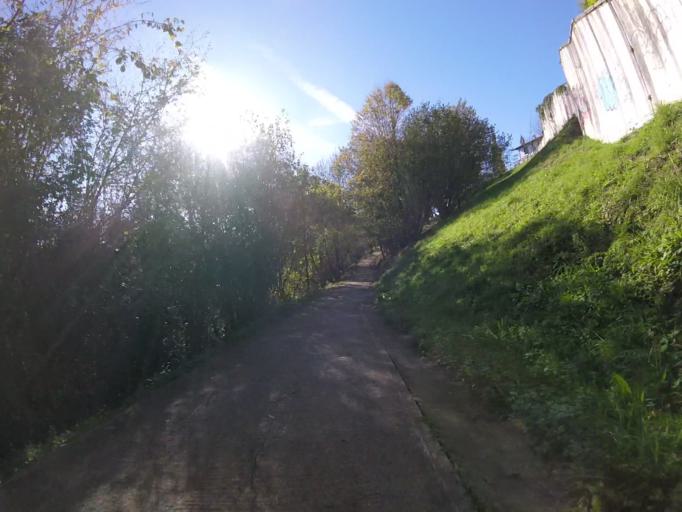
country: ES
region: Basque Country
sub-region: Provincia de Guipuzcoa
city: San Sebastian
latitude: 43.2954
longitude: -1.9889
